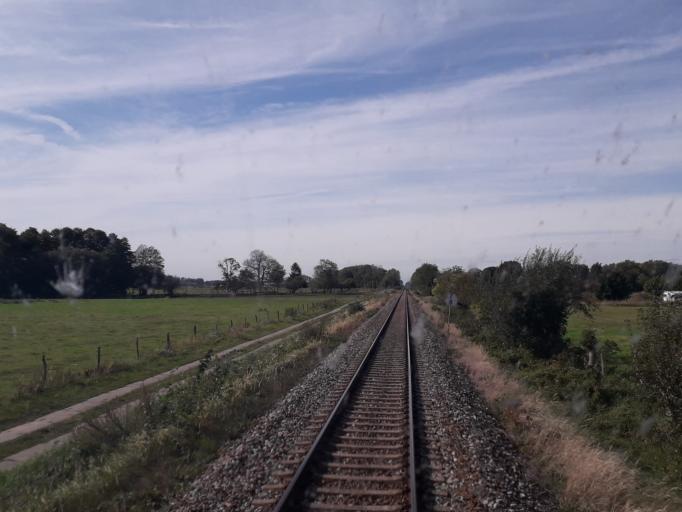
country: DE
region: Brandenburg
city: Kremmen
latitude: 52.8098
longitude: 13.0080
